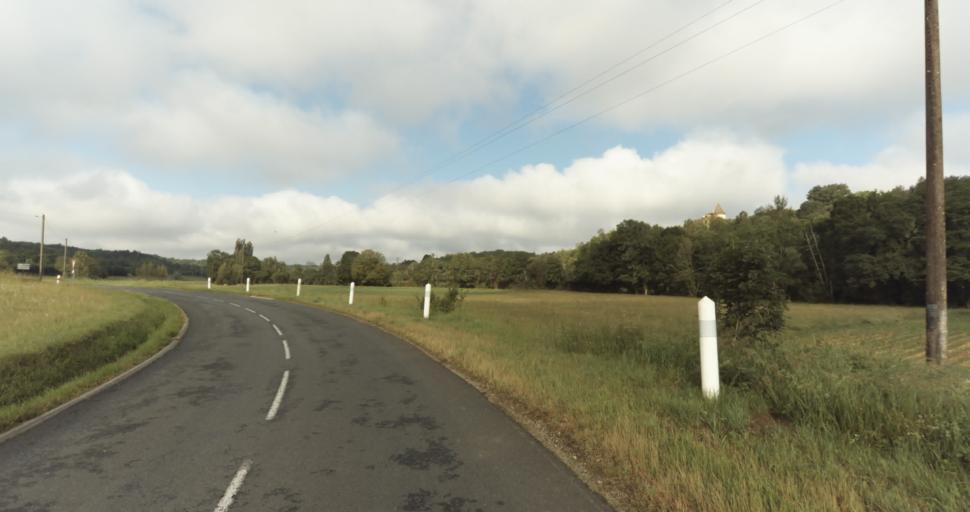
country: FR
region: Aquitaine
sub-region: Departement de la Dordogne
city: Lalinde
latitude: 44.9324
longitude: 0.7665
